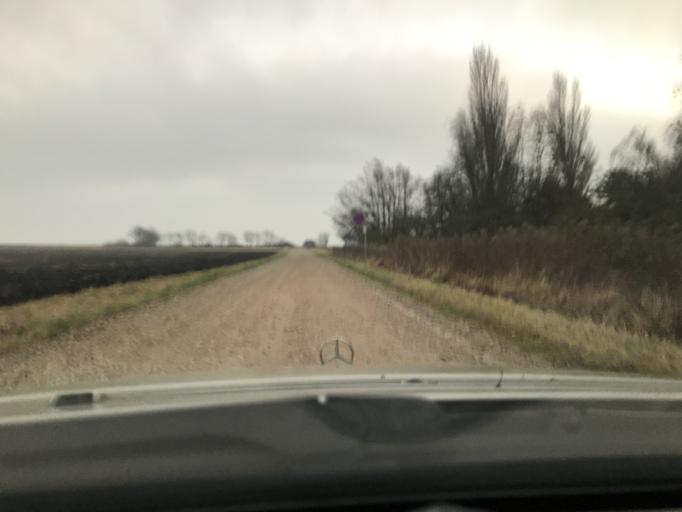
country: DK
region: South Denmark
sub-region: Sonderborg Kommune
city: Horuphav
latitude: 54.8685
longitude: 10.0022
